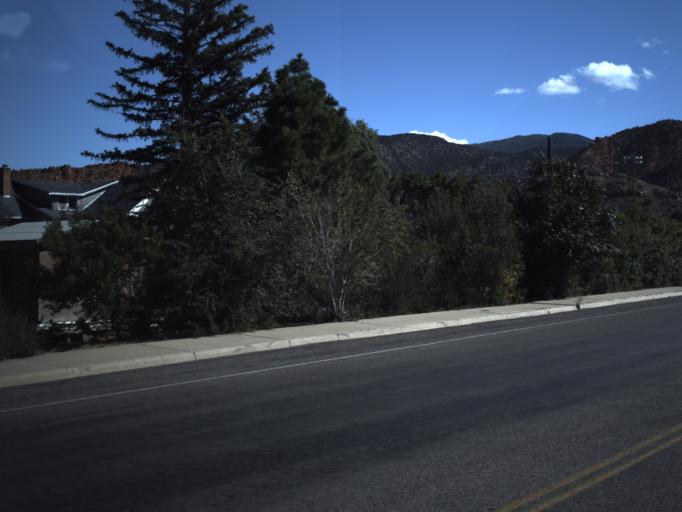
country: US
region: Utah
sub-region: Iron County
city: Cedar City
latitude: 37.6809
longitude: -113.0592
